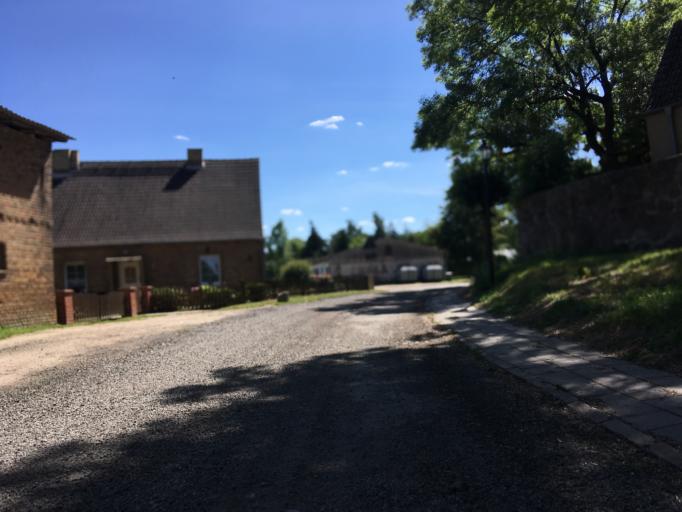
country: DE
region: Brandenburg
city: Brussow
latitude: 53.3226
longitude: 14.1182
